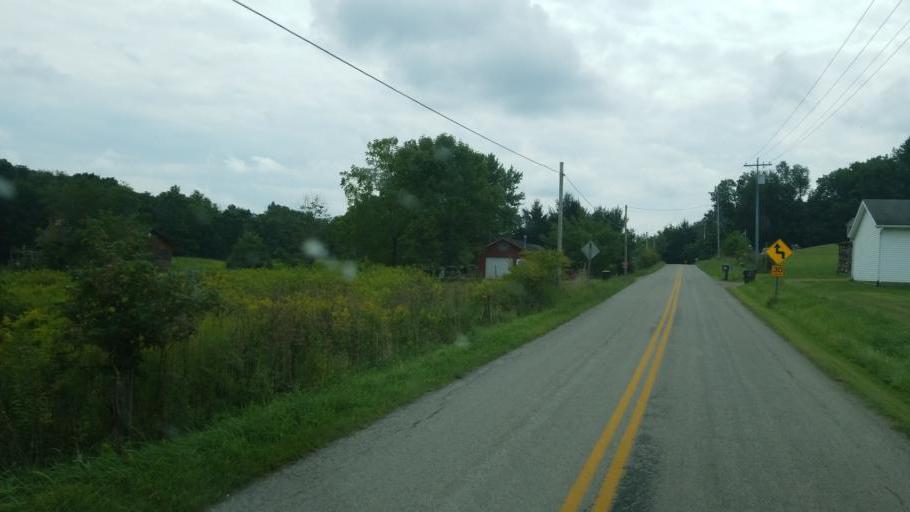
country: US
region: Ohio
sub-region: Ashland County
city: Loudonville
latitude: 40.5672
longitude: -82.3075
